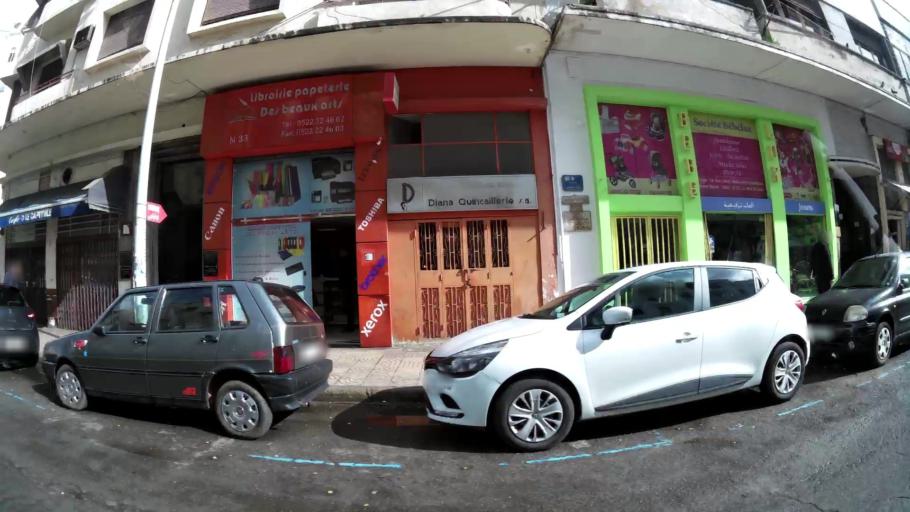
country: MA
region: Grand Casablanca
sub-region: Casablanca
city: Casablanca
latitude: 33.5880
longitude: -7.6191
